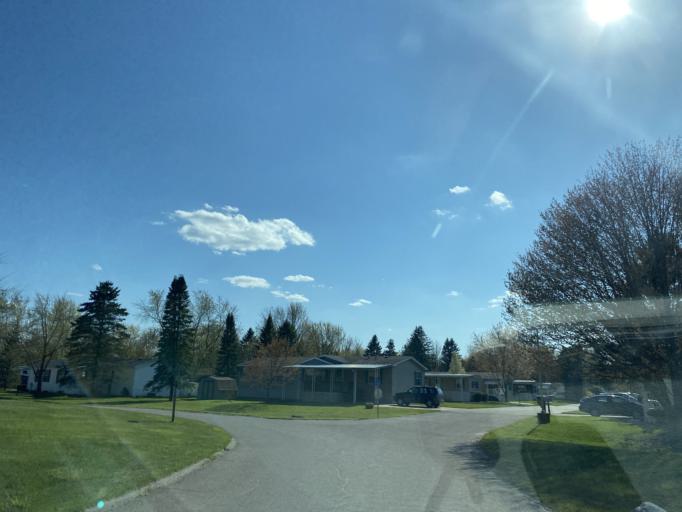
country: US
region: Michigan
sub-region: Livingston County
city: Brighton
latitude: 42.5686
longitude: -83.8231
